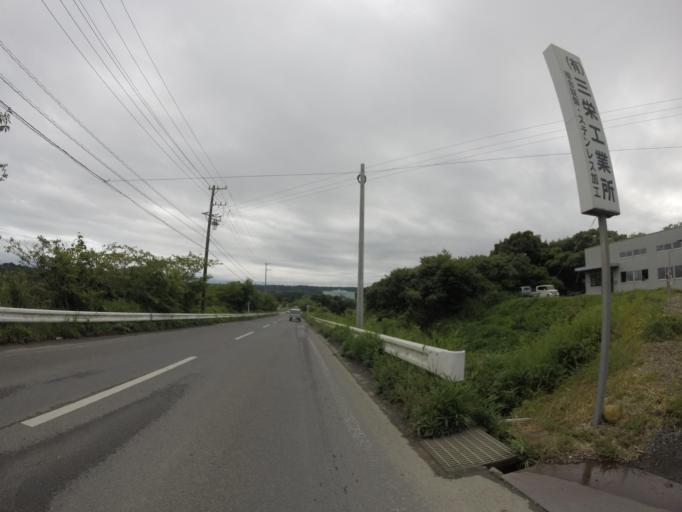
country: JP
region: Shizuoka
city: Sagara
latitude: 34.7365
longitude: 138.1878
